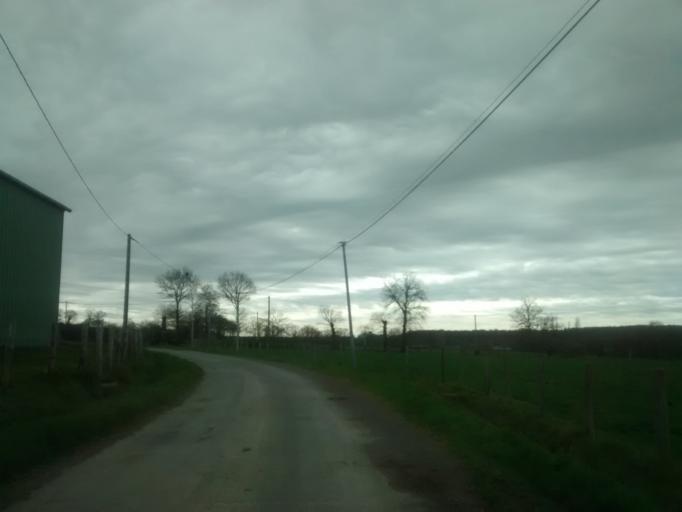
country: FR
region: Brittany
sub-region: Departement d'Ille-et-Vilaine
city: Gosne
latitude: 48.2440
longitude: -1.4752
